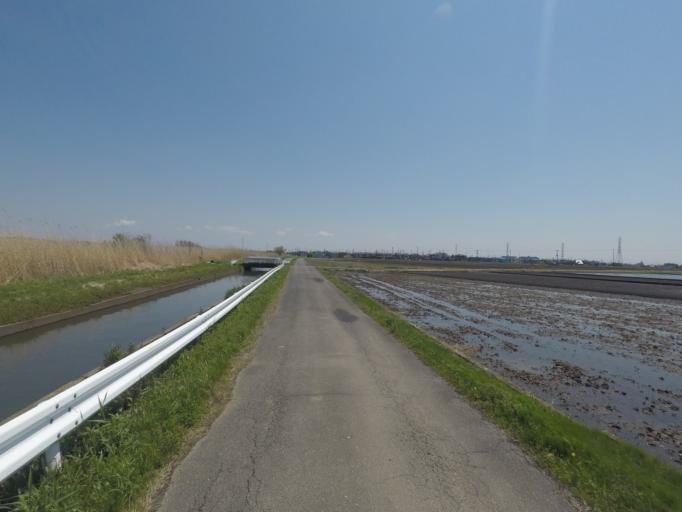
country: JP
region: Ibaraki
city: Fujishiro
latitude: 35.9431
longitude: 140.1178
